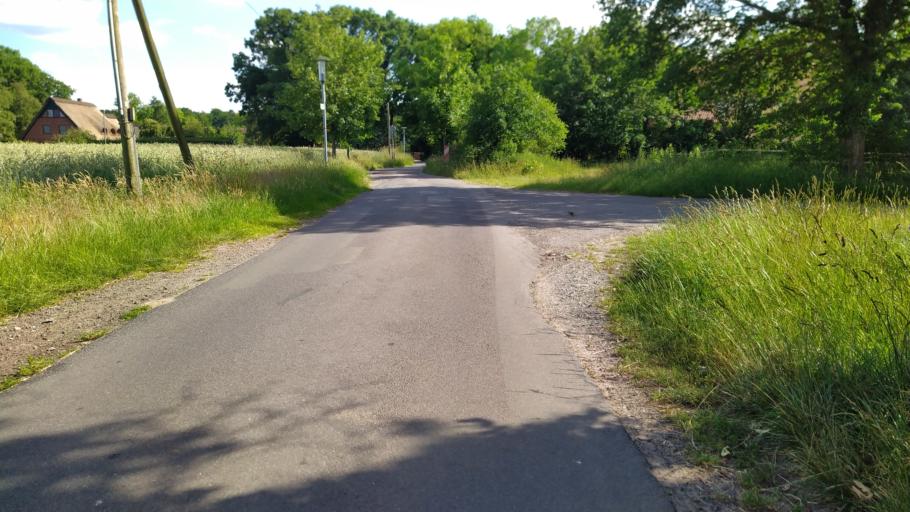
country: DE
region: Lower Saxony
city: Lintig
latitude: 53.6299
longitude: 8.8959
